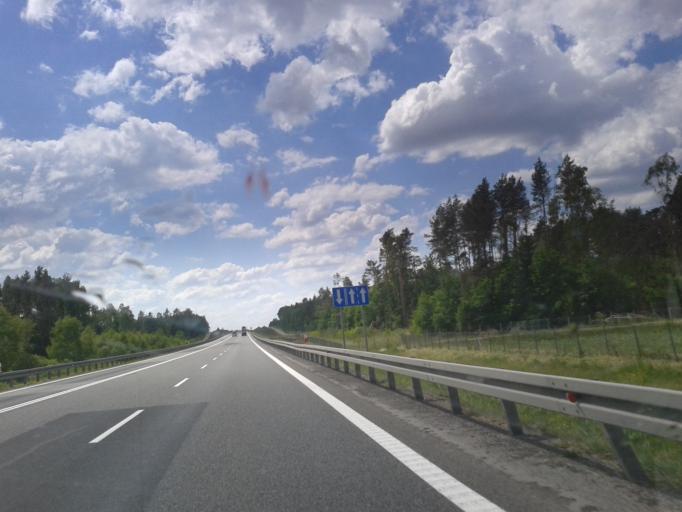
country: PL
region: Pomeranian Voivodeship
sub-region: Powiat chojnicki
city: Chojnice
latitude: 53.7043
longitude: 17.6365
